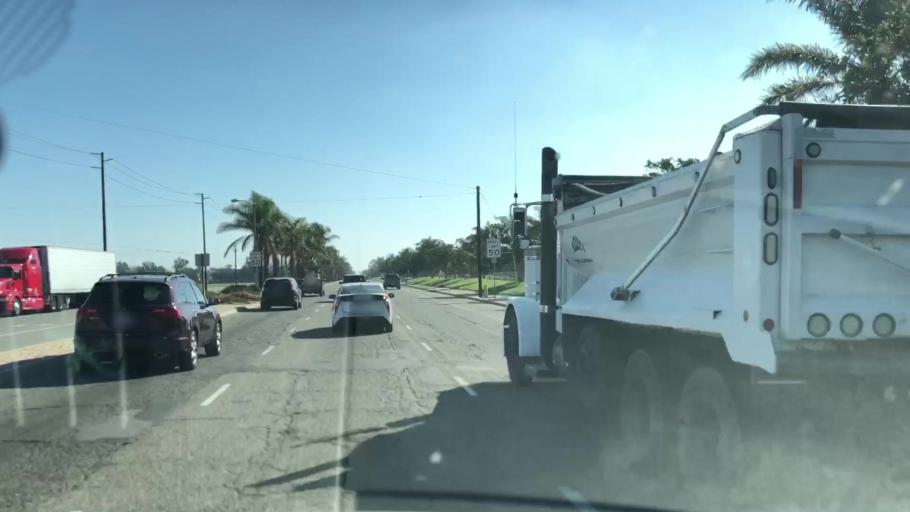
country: US
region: California
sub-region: Ventura County
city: El Rio
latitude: 34.2182
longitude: -119.1421
